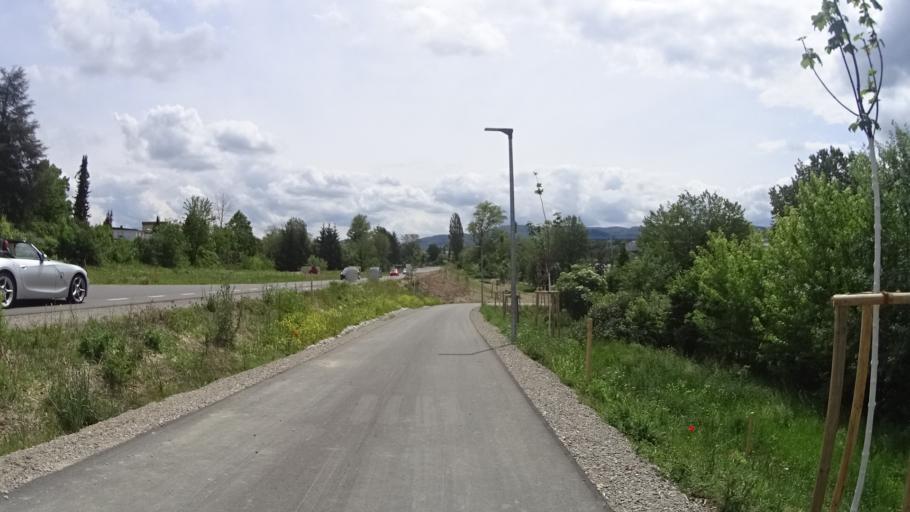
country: CH
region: Basel-Landschaft
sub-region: Bezirk Arlesheim
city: Birsfelden
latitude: 47.5579
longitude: 7.6430
